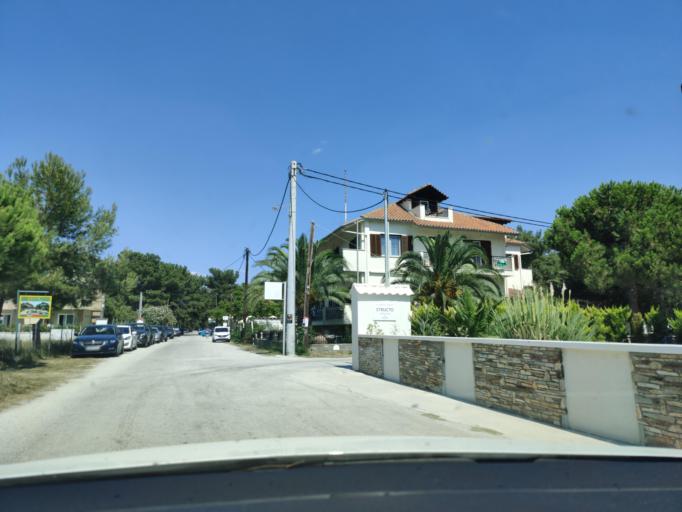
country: GR
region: East Macedonia and Thrace
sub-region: Nomos Kavalas
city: Prinos
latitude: 40.7587
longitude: 24.5617
